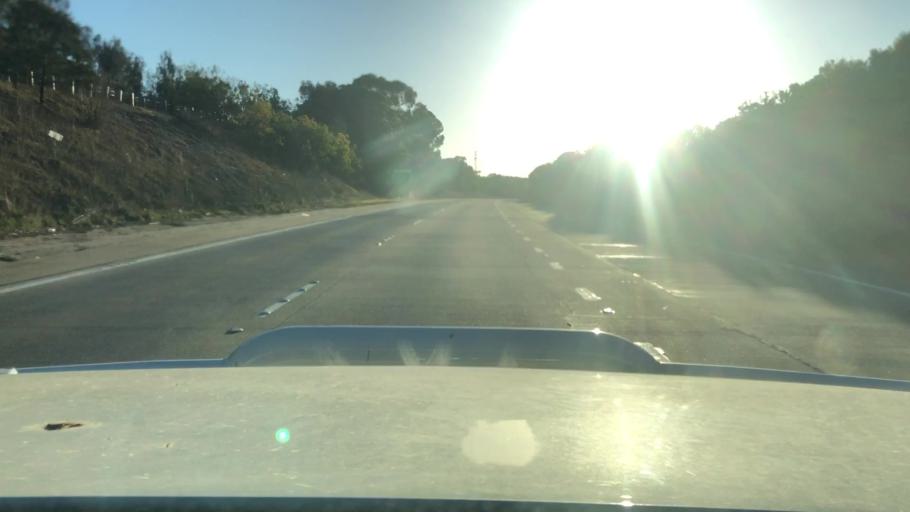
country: AU
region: New South Wales
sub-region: Wingecarribee
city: Bundanoon
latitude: -34.6958
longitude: 150.0240
